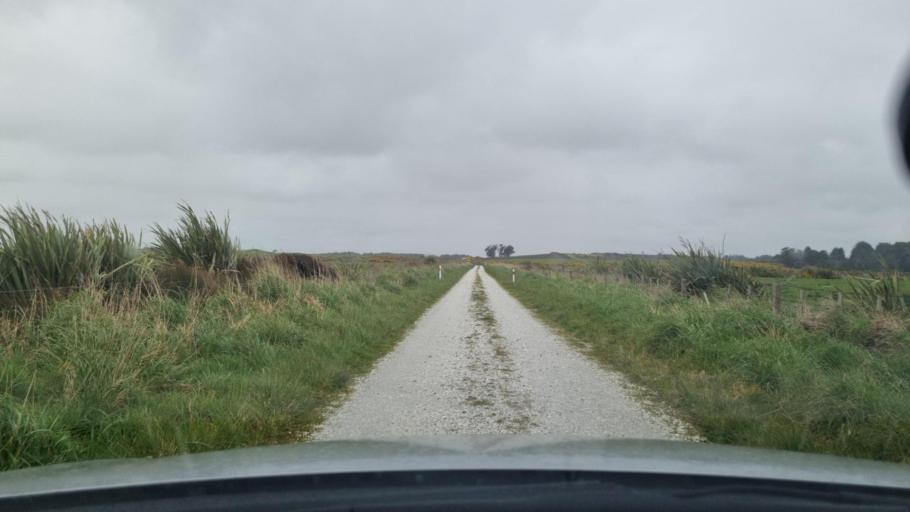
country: NZ
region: Southland
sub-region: Invercargill City
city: Bluff
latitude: -46.5202
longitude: 168.2779
